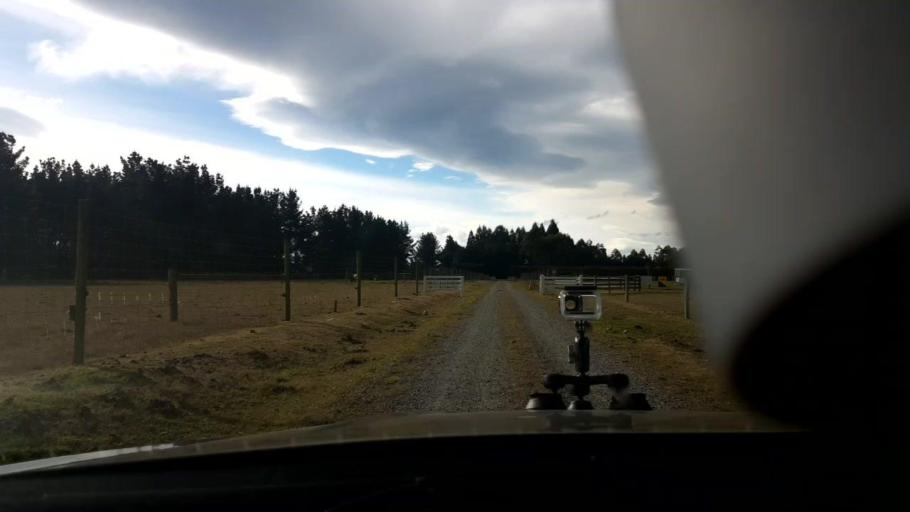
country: NZ
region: Canterbury
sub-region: Waimakariri District
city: Oxford
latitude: -43.4012
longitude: 172.3120
